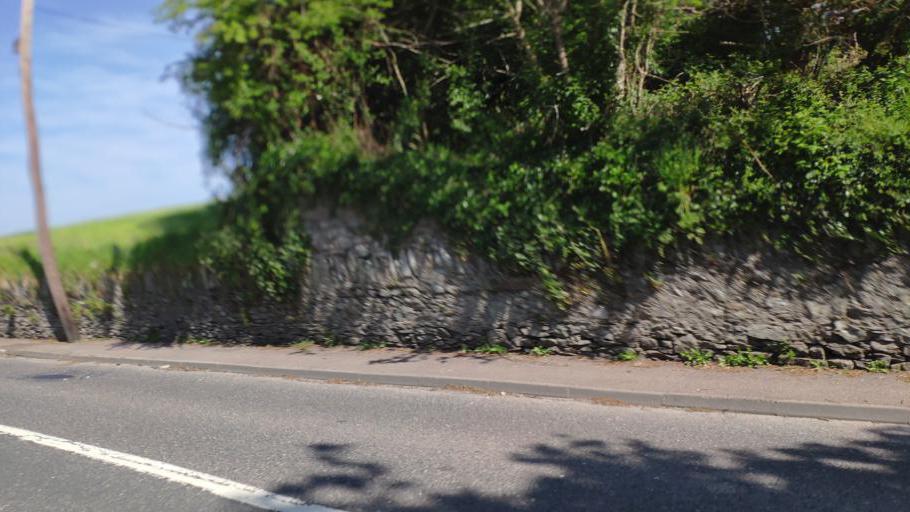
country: IE
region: Munster
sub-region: County Cork
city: Blarney
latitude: 51.9314
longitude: -8.5548
